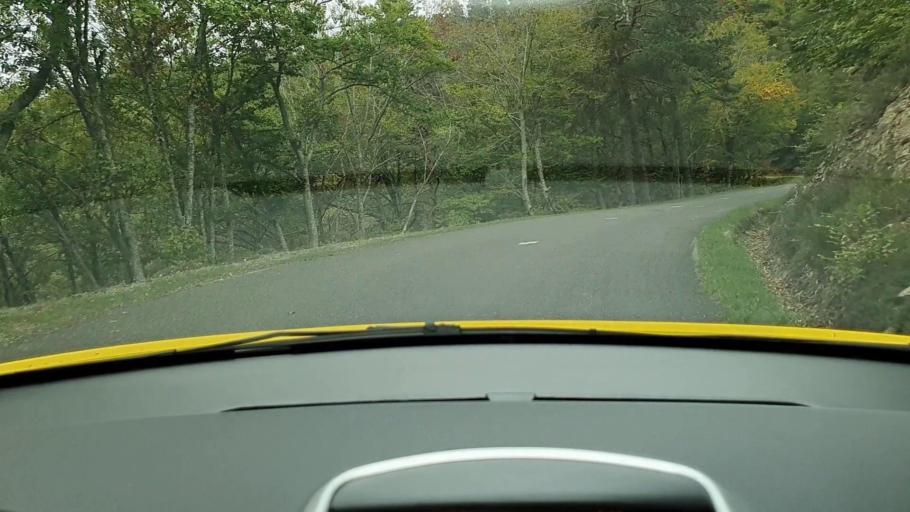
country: FR
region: Languedoc-Roussillon
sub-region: Departement de la Lozere
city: Meyrueis
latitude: 44.0826
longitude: 3.4161
